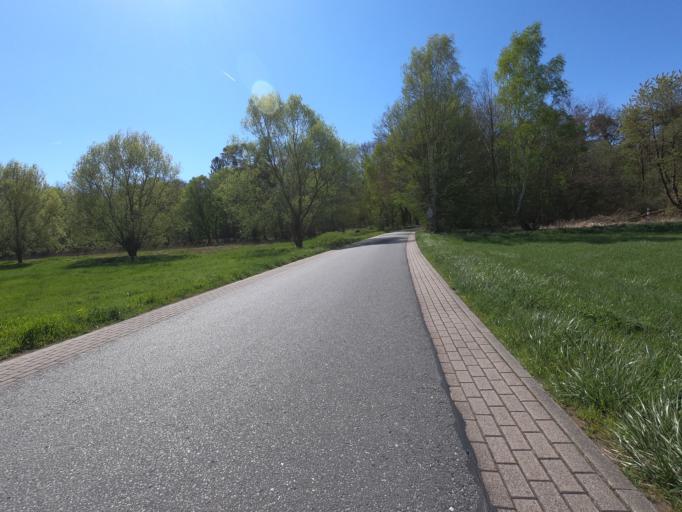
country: DE
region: Hesse
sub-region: Regierungsbezirk Darmstadt
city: Erzhausen
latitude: 49.9477
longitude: 8.6155
